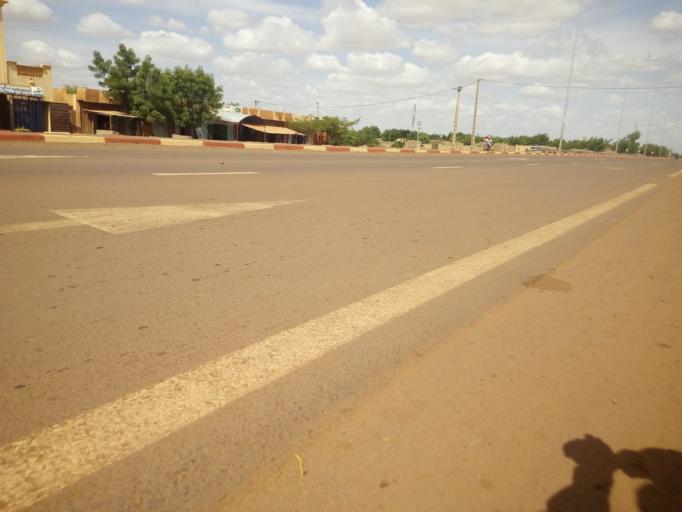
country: ML
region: Segou
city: Segou
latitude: 13.4276
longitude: -6.2211
